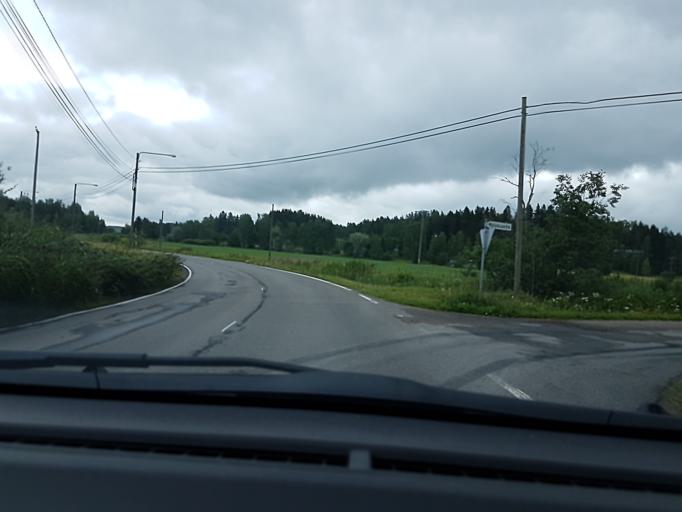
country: FI
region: Uusimaa
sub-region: Helsinki
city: Pornainen
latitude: 60.4350
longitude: 25.3855
